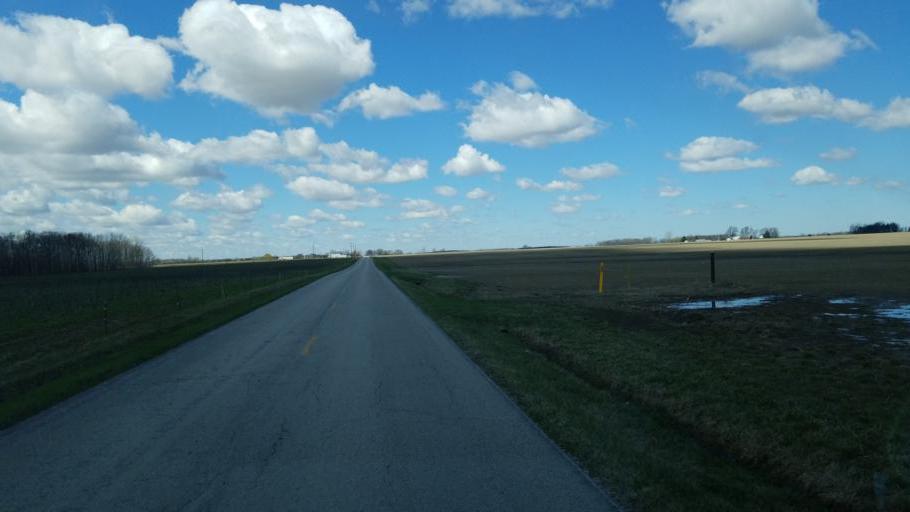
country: US
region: Ohio
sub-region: Sandusky County
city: Mount Carmel
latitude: 41.2418
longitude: -82.9846
